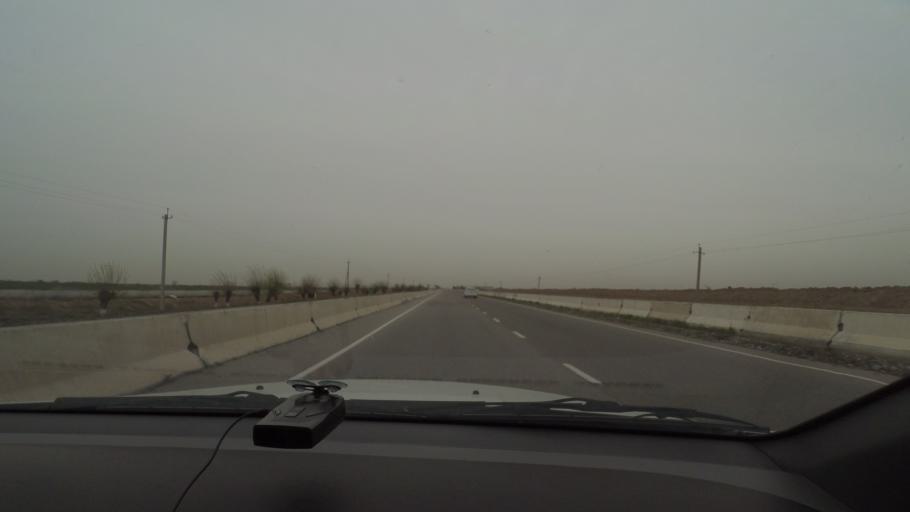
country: UZ
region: Jizzax
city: Gagarin
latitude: 40.4656
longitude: 68.2669
